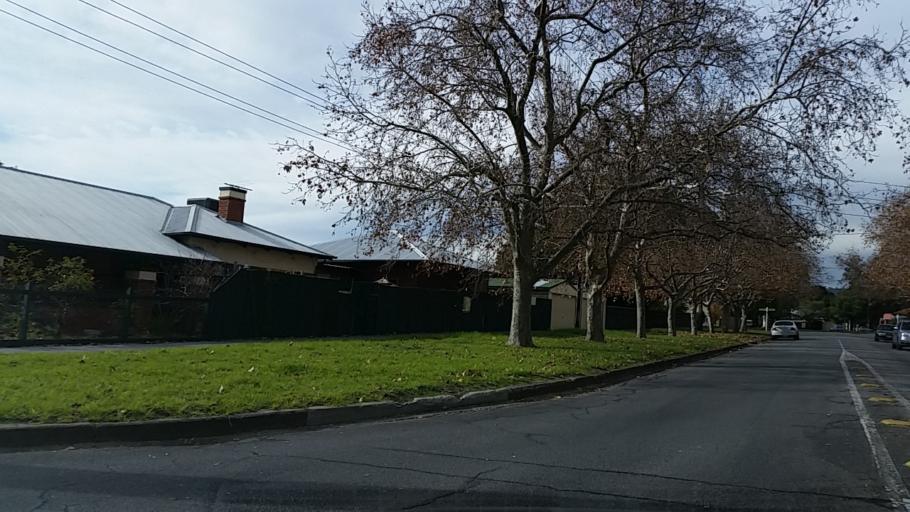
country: AU
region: South Australia
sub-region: Mitcham
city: Clapham
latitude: -34.9837
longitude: 138.5909
